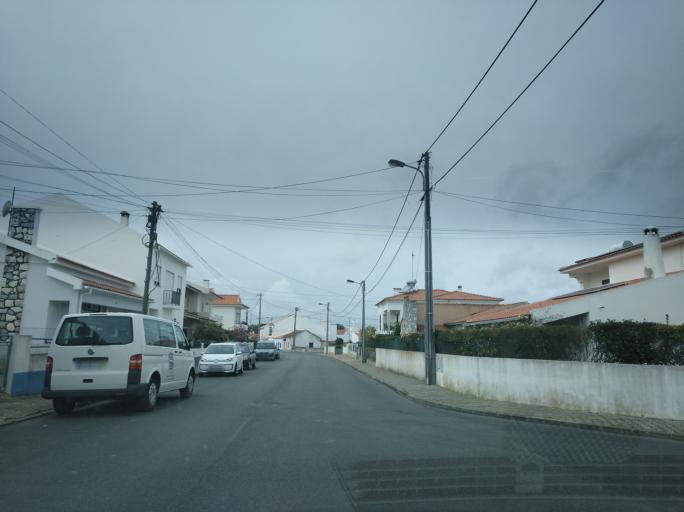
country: PT
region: Setubal
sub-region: Grandola
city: Grandola
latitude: 38.1786
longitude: -8.5699
